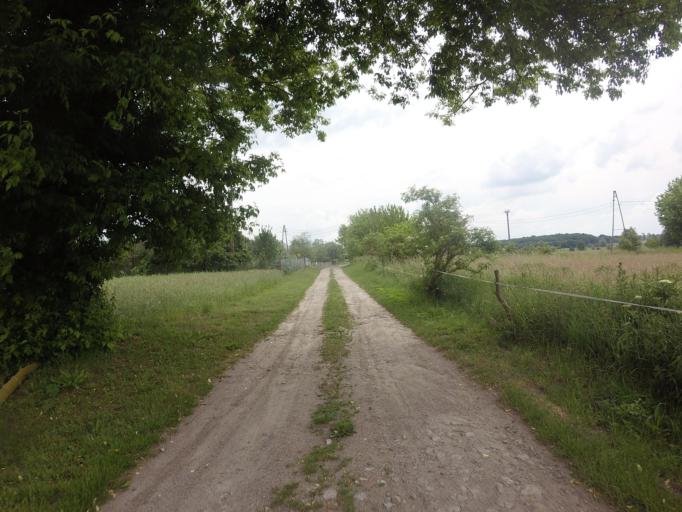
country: PL
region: West Pomeranian Voivodeship
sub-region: Powiat stargardzki
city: Dobrzany
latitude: 53.3225
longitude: 15.4788
